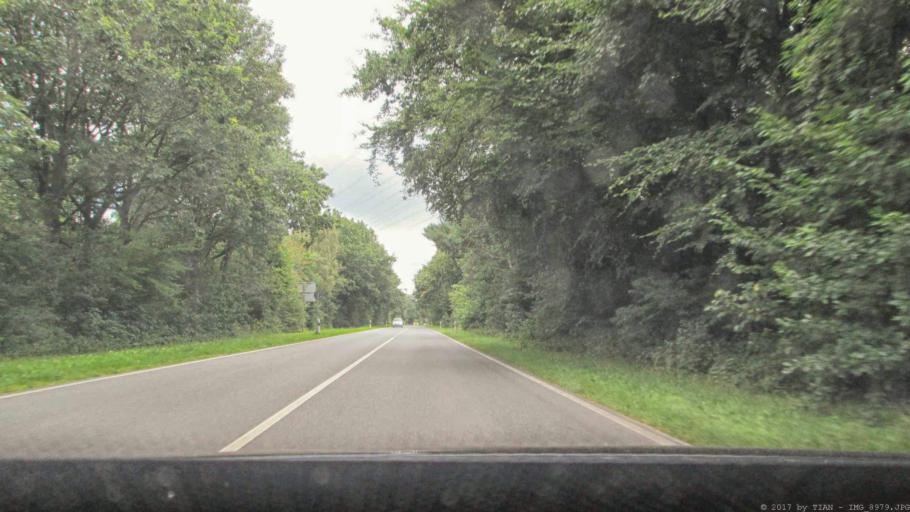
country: DE
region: Schleswig-Holstein
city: Tangstedt
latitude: 53.7284
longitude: 10.0255
